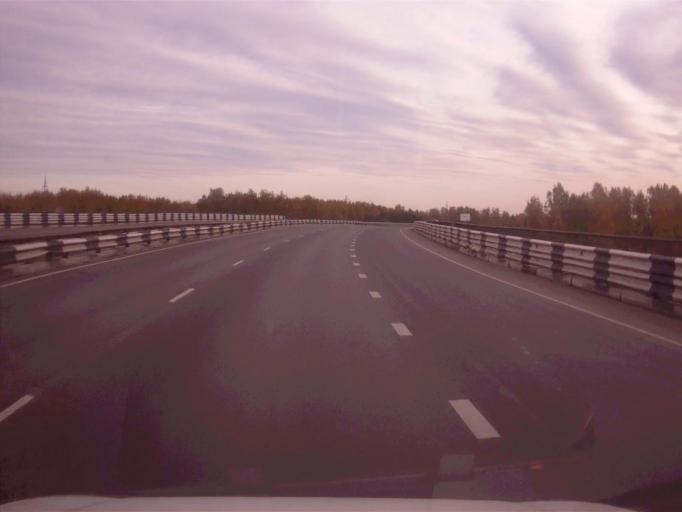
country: RU
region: Chelyabinsk
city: Novosineglazovskiy
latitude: 55.0401
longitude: 61.4392
